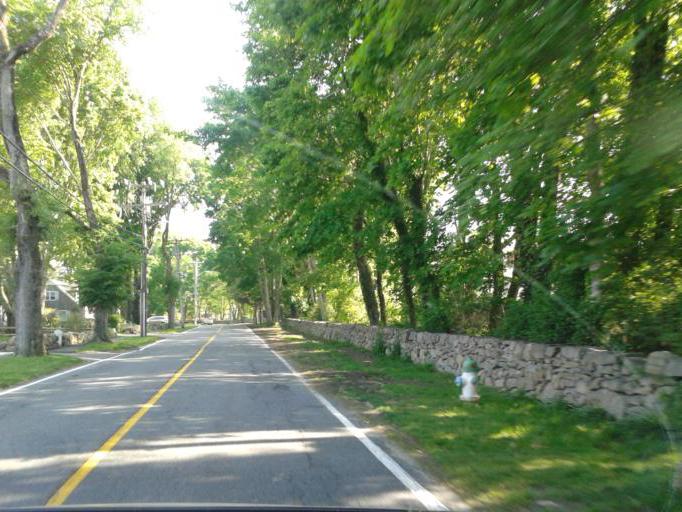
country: US
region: Massachusetts
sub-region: Barnstable County
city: Falmouth
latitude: 41.5496
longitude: -70.6271
